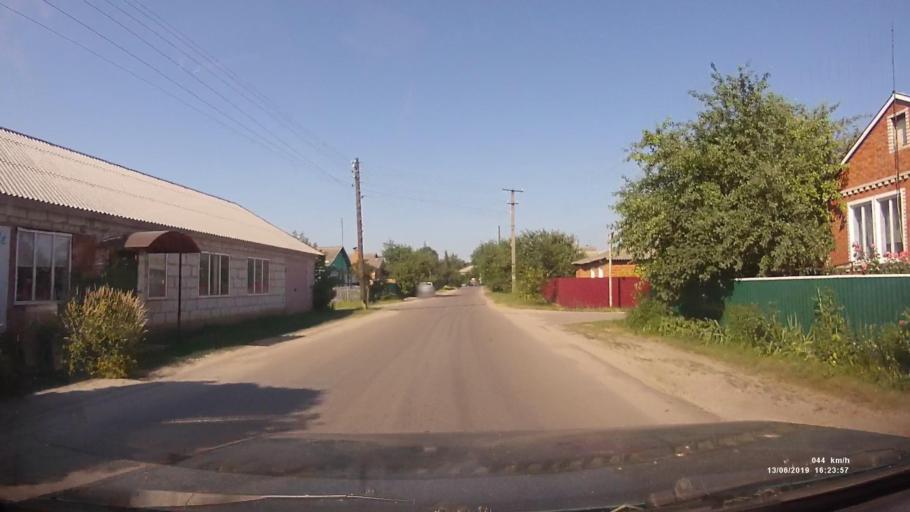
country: RU
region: Rostov
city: Kazanskaya
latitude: 49.7963
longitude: 41.1441
